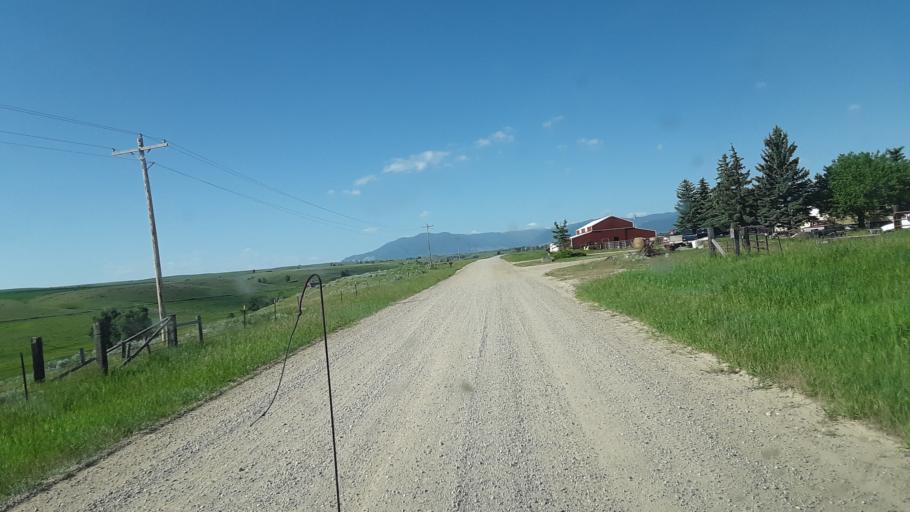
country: US
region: Montana
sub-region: Carbon County
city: Red Lodge
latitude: 45.3372
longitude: -109.1622
